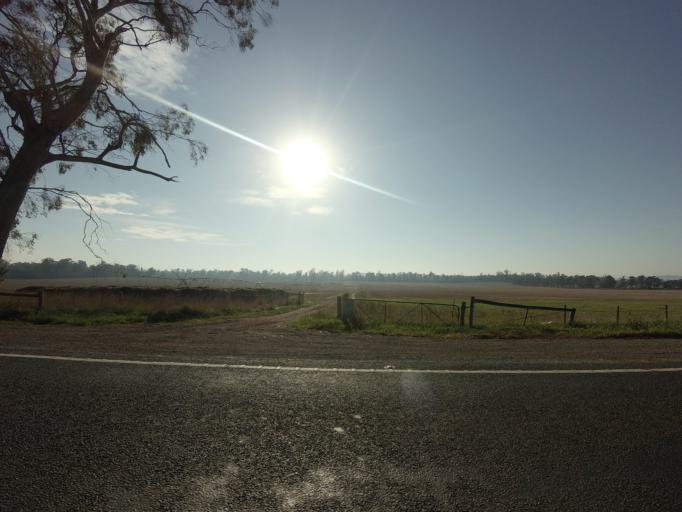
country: AU
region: Tasmania
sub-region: Northern Midlands
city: Longford
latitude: -41.5415
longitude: 147.0535
